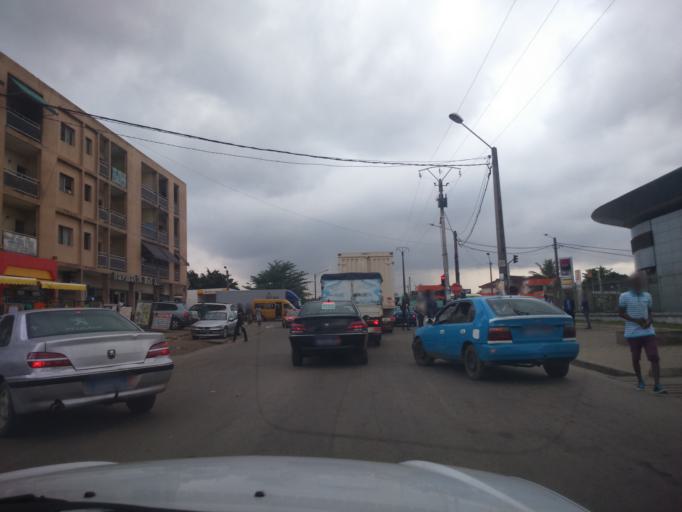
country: CI
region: Lagunes
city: Abidjan
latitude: 5.3467
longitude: -4.0640
